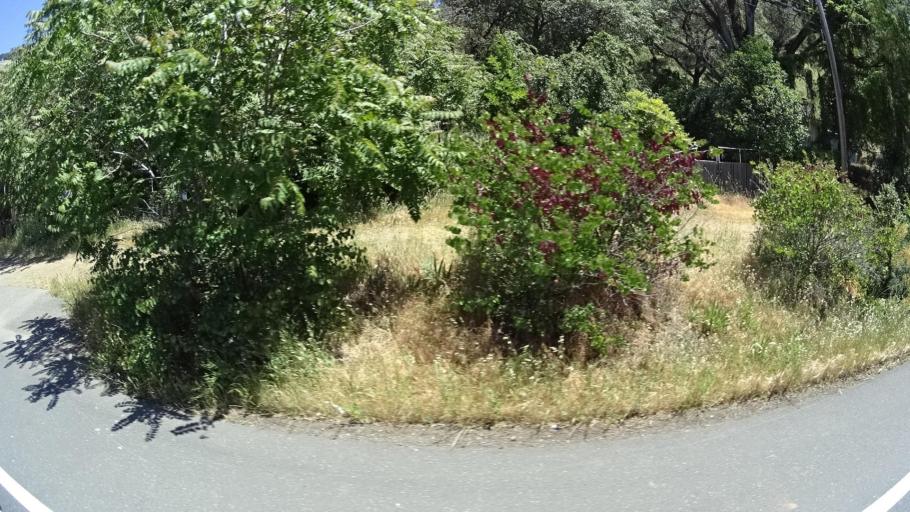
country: US
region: California
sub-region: Lake County
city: Lucerne
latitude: 39.0567
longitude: -122.7816
